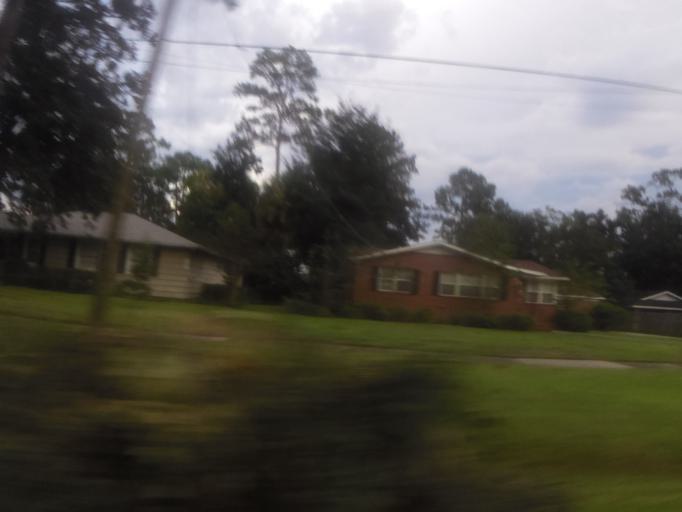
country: US
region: Florida
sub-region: Duval County
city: Jacksonville
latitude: 30.2553
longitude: -81.6977
